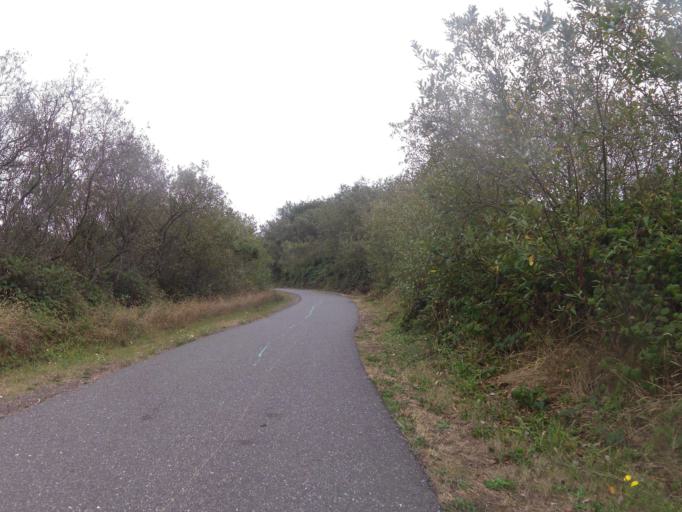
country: US
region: California
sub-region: Humboldt County
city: Bayview
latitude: 40.7678
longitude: -124.1966
